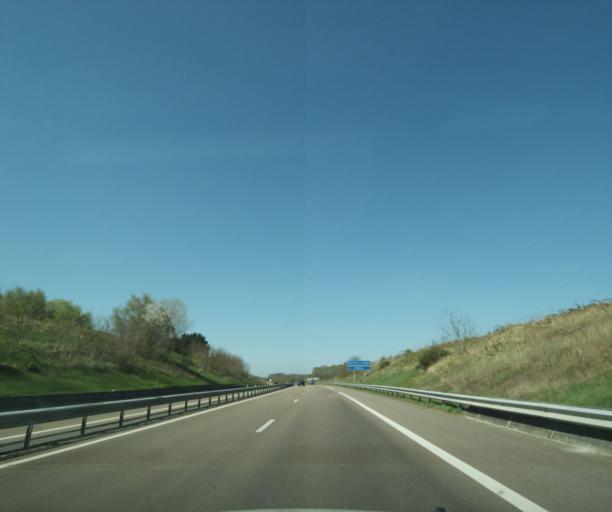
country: FR
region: Bourgogne
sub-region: Departement de la Nievre
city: Cosne-Cours-sur-Loire
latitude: 47.4161
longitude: 2.9463
